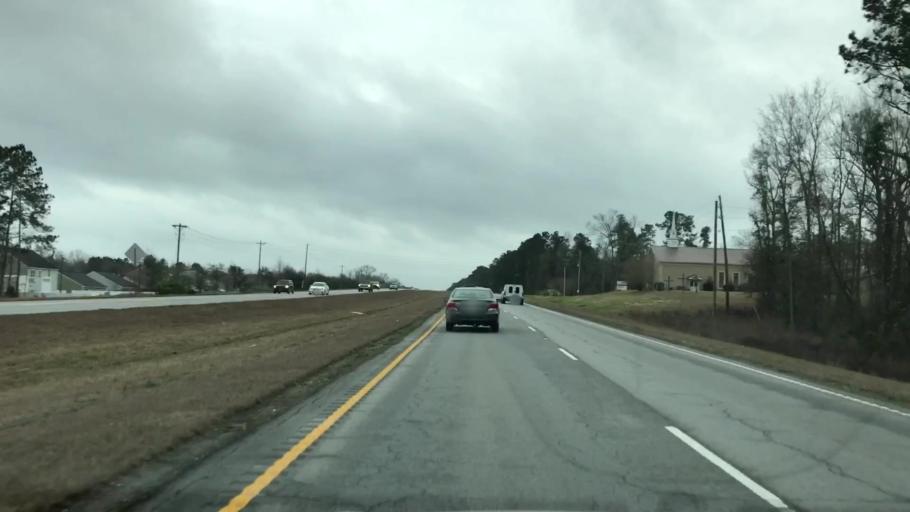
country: US
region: South Carolina
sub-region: Berkeley County
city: Moncks Corner
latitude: 33.1380
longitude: -80.0321
